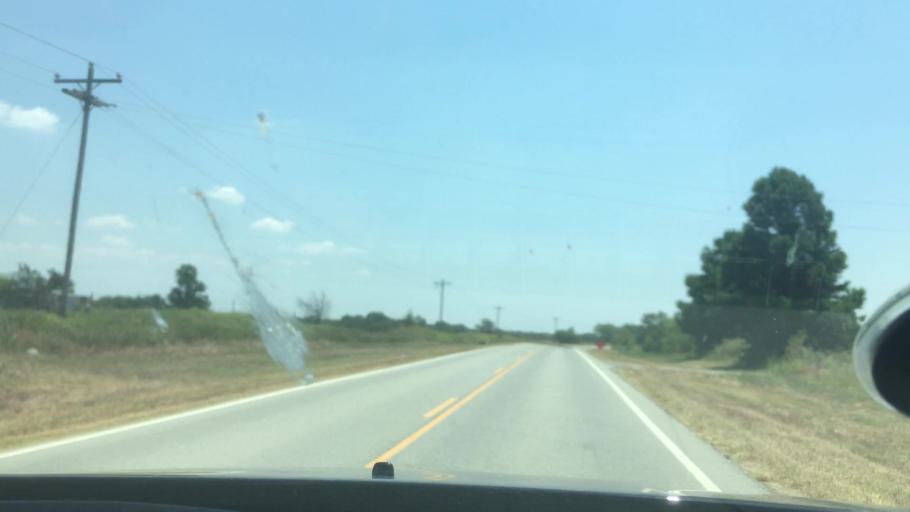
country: US
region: Oklahoma
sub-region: Coal County
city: Coalgate
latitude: 34.5810
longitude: -96.4102
